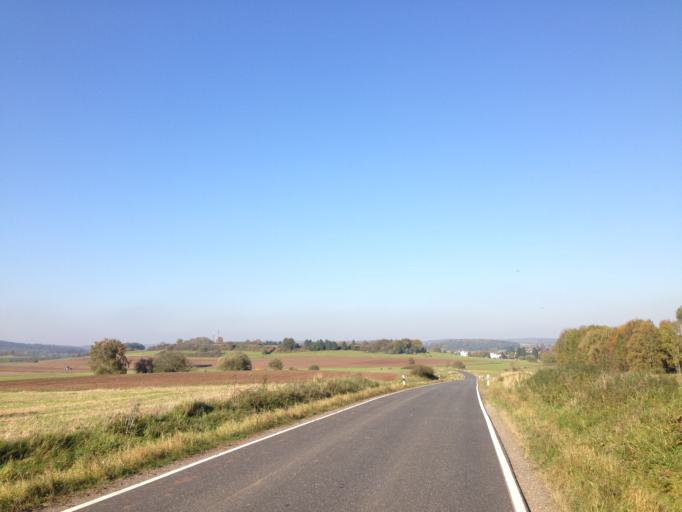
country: DE
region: Hesse
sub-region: Regierungsbezirk Giessen
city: Reiskirchen
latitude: 50.5669
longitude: 8.8101
